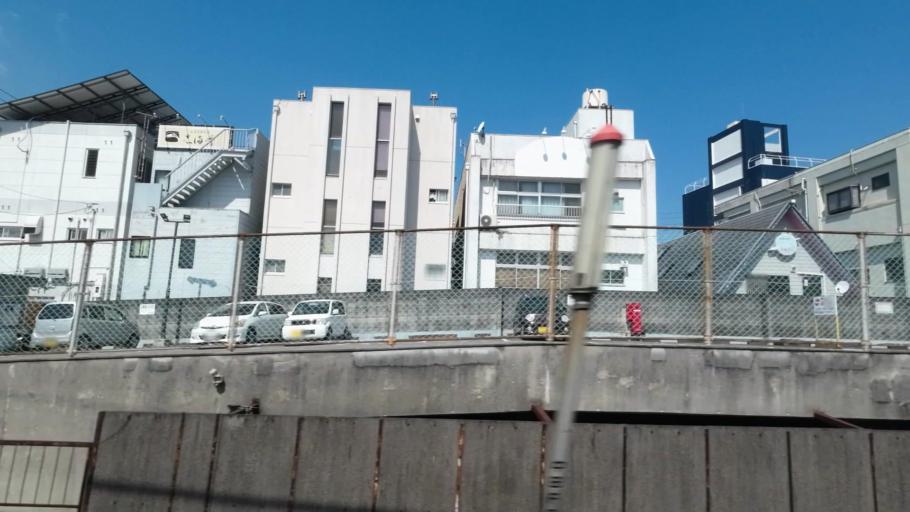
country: JP
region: Ehime
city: Kawanoecho
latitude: 34.0115
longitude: 133.5754
